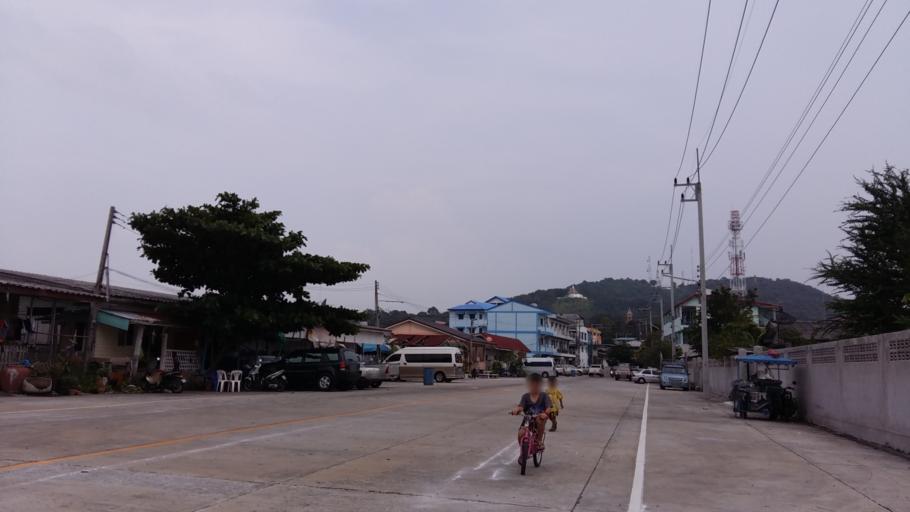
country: TH
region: Chon Buri
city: Chon Buri
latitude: 13.3924
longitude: 100.9847
